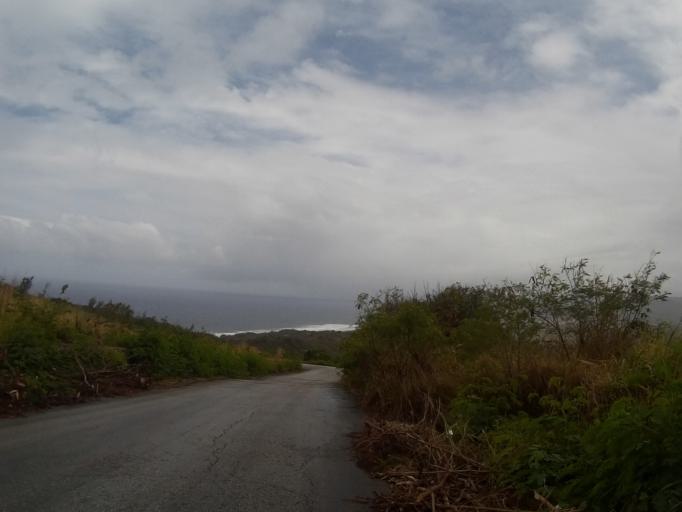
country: BB
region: Saint Andrew
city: Greenland
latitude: 13.2748
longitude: -59.5799
